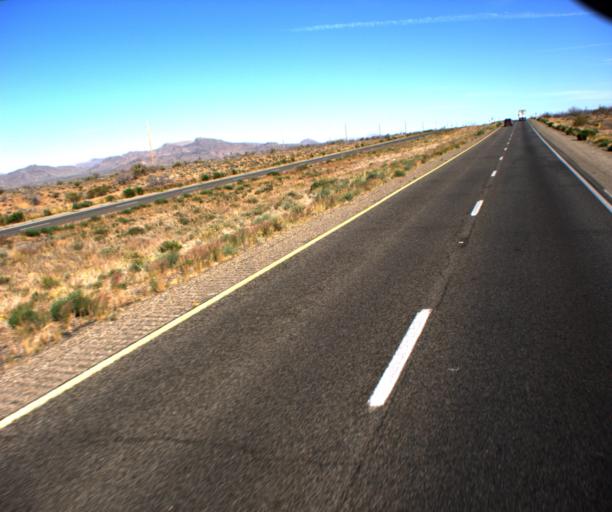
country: US
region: Arizona
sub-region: Mohave County
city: Golden Valley
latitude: 35.3062
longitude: -114.1935
